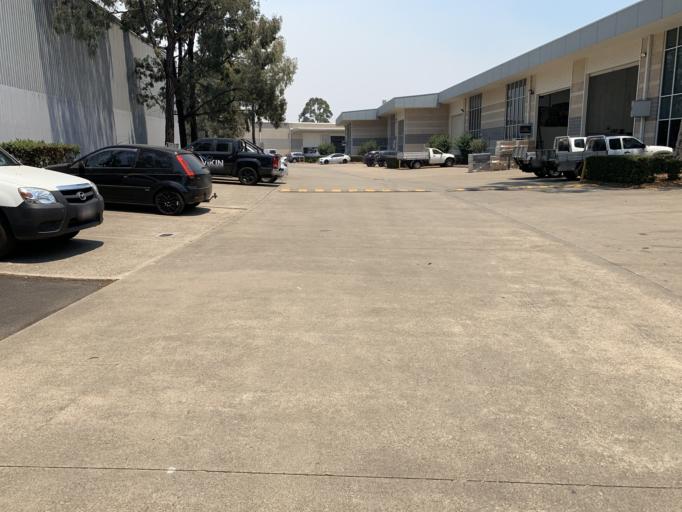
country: AU
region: New South Wales
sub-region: Holroyd
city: Girraween
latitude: -33.7732
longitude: 150.9519
